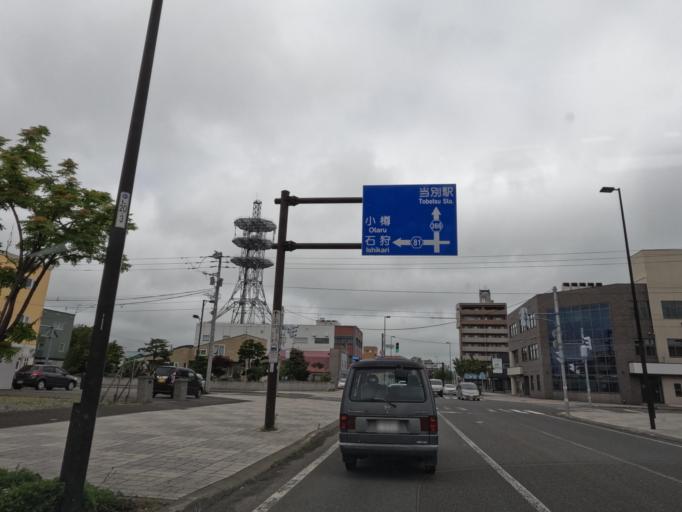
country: JP
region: Hokkaido
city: Tobetsu
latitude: 43.2194
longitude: 141.5153
